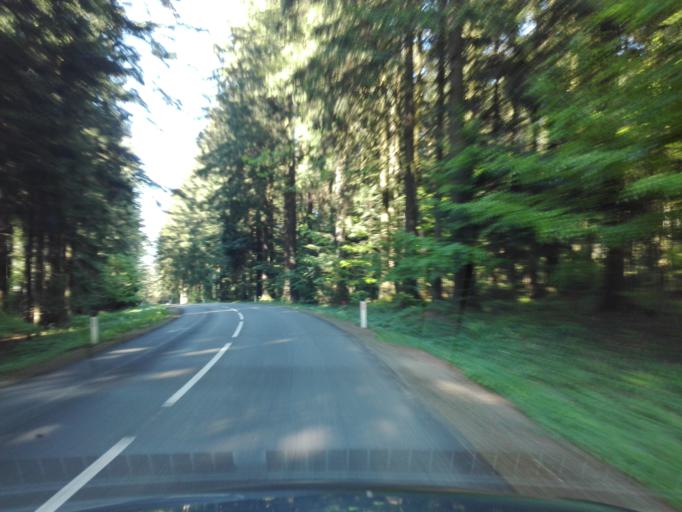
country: DE
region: Bavaria
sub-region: Lower Bavaria
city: Obernzell
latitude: 48.5226
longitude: 13.6376
